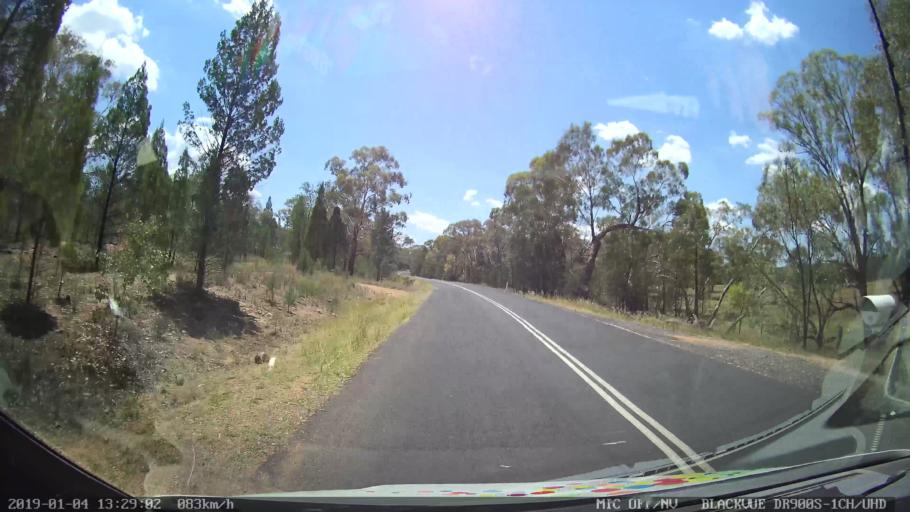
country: AU
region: New South Wales
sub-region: Parkes
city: Peak Hill
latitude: -32.6516
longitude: 148.5507
